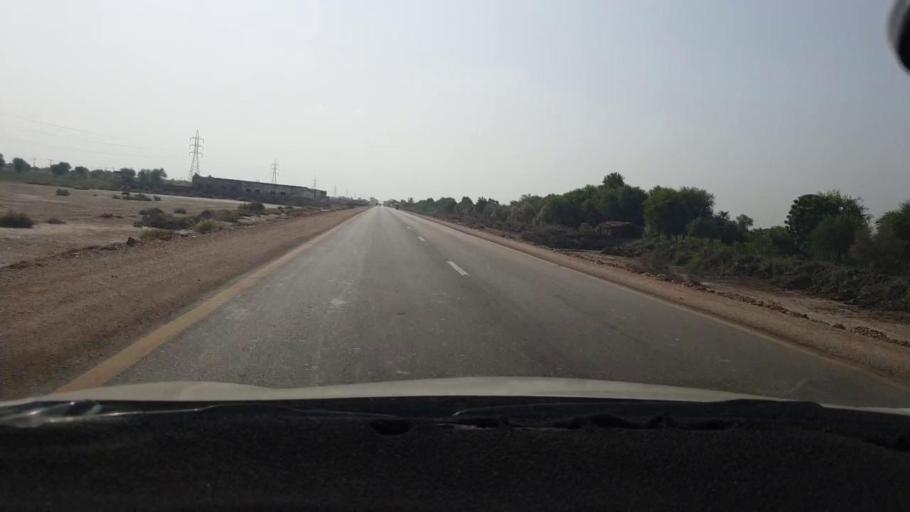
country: PK
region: Sindh
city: Jhol
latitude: 25.9151
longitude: 69.0095
